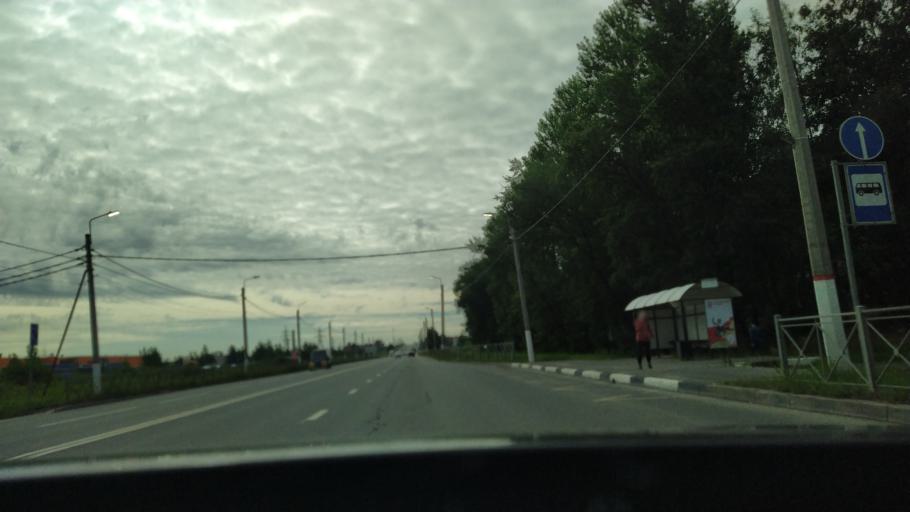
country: RU
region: Leningrad
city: Tosno
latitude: 59.5565
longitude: 30.8484
